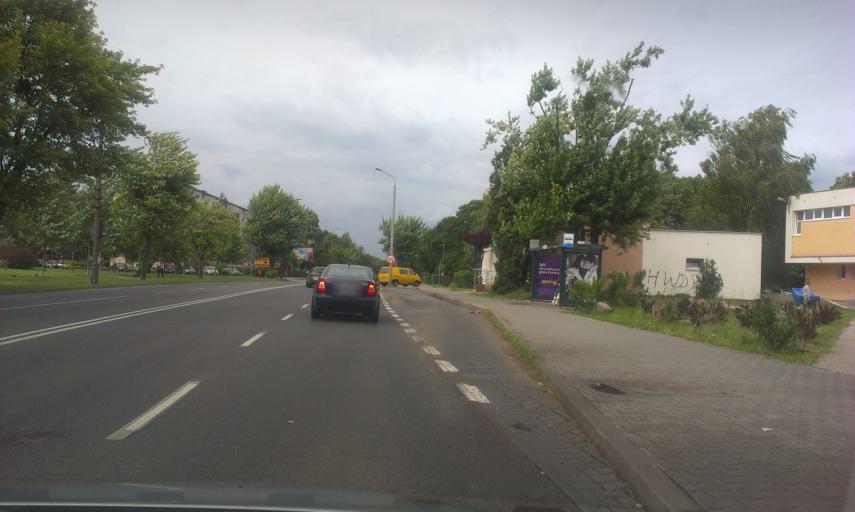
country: PL
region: Greater Poland Voivodeship
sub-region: Poznan
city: Poznan
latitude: 52.4069
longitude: 16.8754
